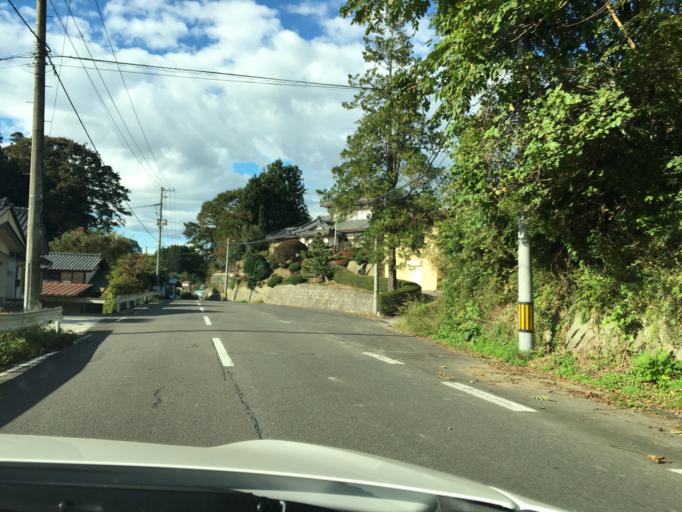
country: JP
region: Fukushima
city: Sukagawa
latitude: 37.2495
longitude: 140.4407
